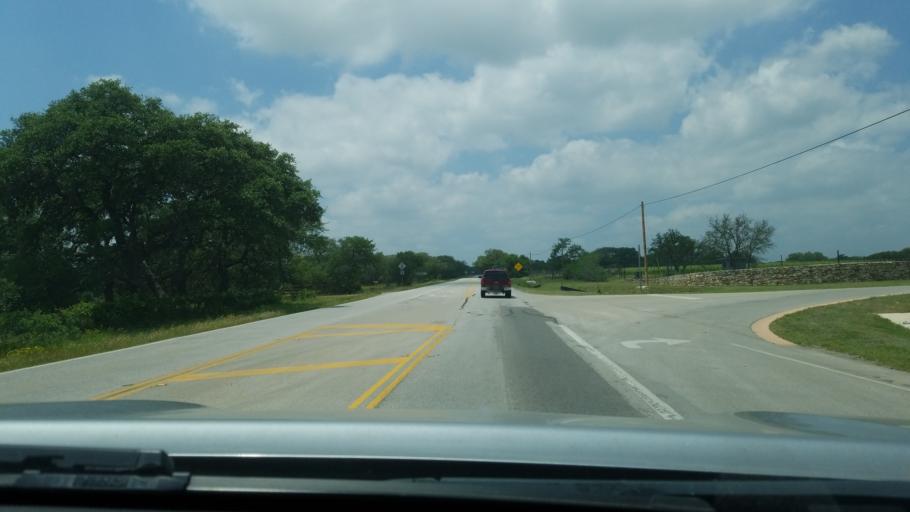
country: US
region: Texas
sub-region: Hays County
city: Dripping Springs
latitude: 30.1316
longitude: -98.0252
